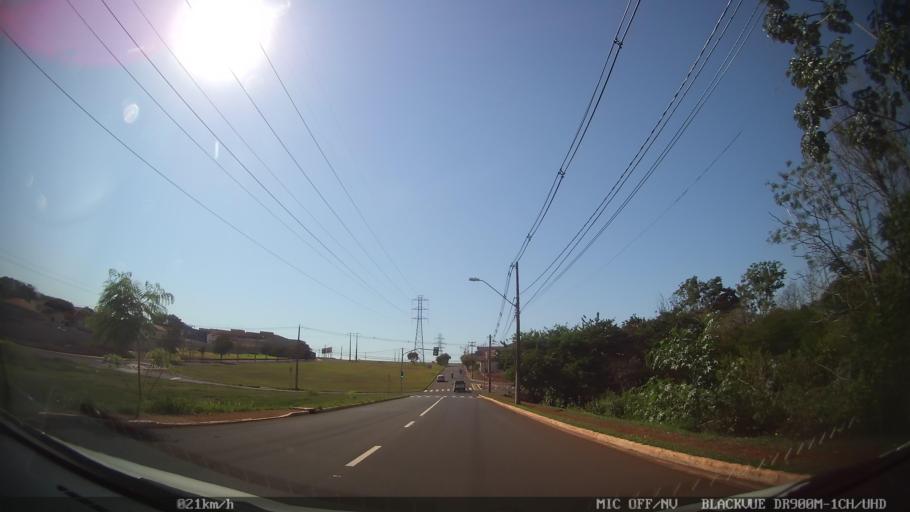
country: BR
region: Sao Paulo
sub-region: Ribeirao Preto
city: Ribeirao Preto
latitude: -21.2188
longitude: -47.7917
